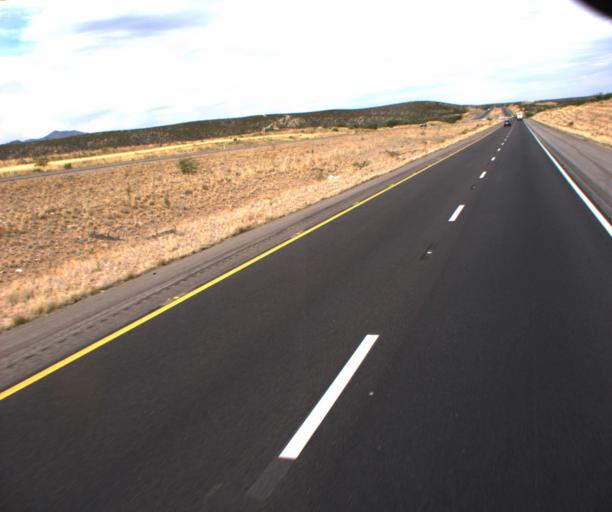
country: US
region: Arizona
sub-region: Cochise County
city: Mescal
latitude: 31.9852
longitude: -110.5606
